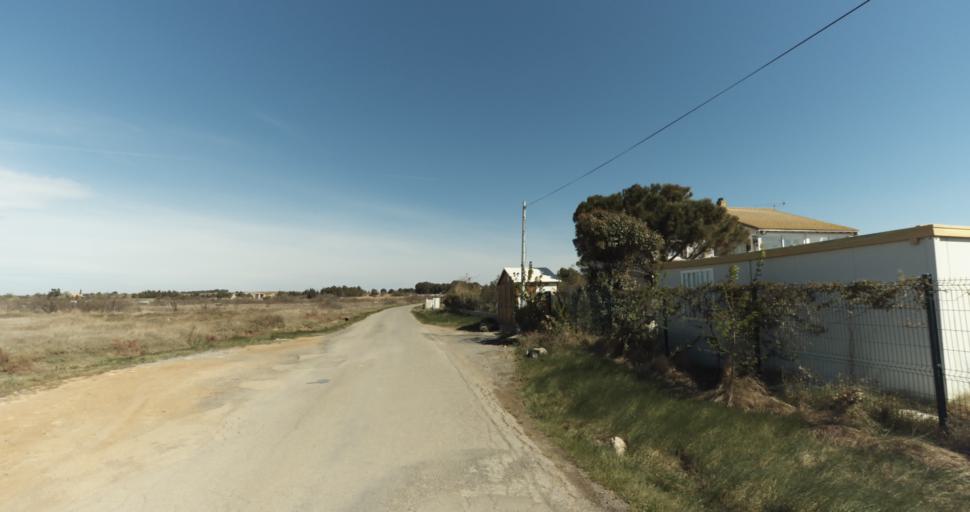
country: FR
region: Languedoc-Roussillon
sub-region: Departement de l'Herault
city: Marseillan
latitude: 43.3636
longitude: 3.5353
